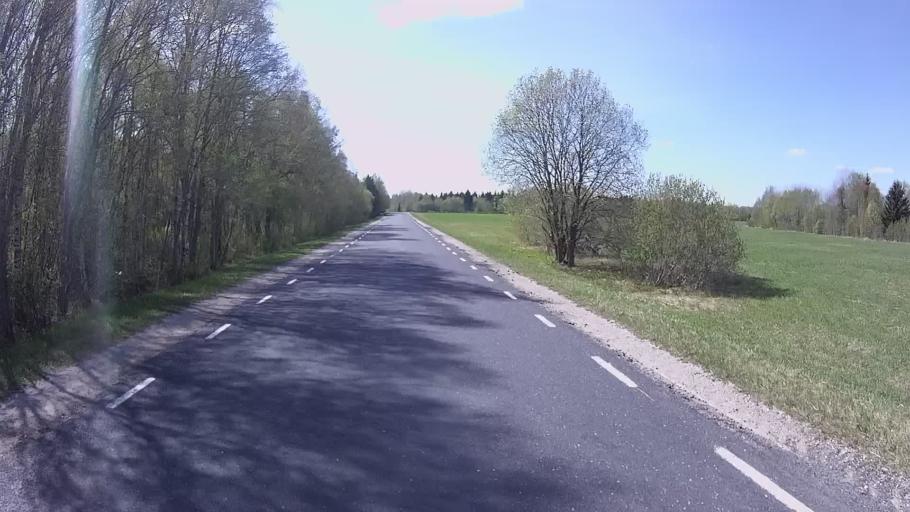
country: EE
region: Laeaene
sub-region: Ridala Parish
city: Uuemoisa
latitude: 59.0149
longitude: 23.7899
